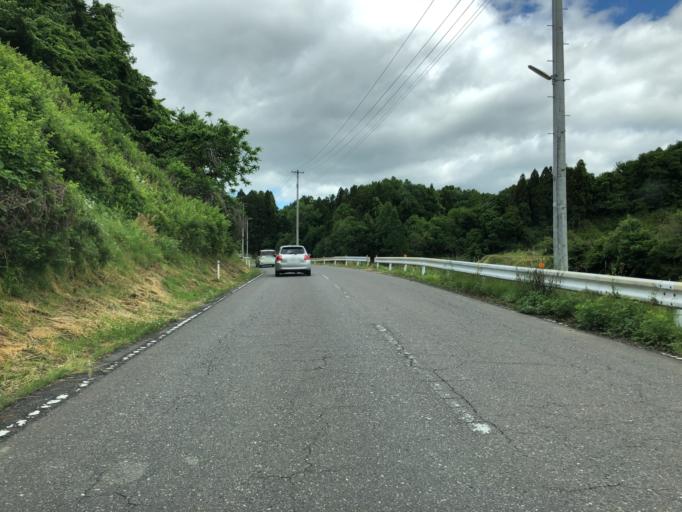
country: JP
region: Fukushima
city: Motomiya
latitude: 37.4792
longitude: 140.4429
